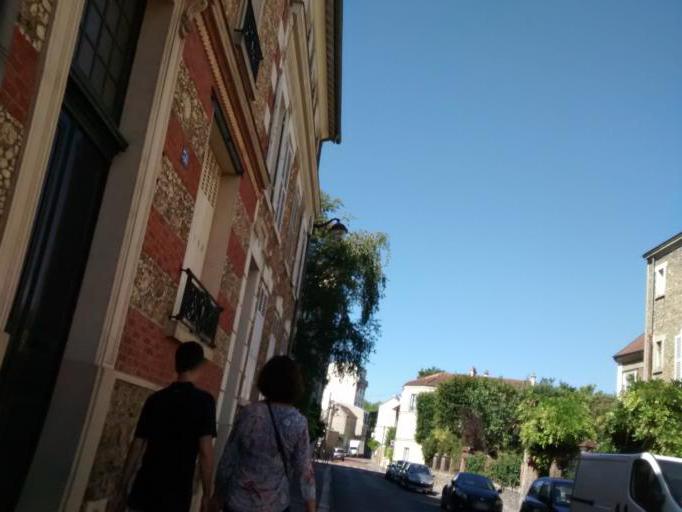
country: FR
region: Ile-de-France
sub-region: Departement des Yvelines
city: Viroflay
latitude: 48.8062
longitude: 2.1479
